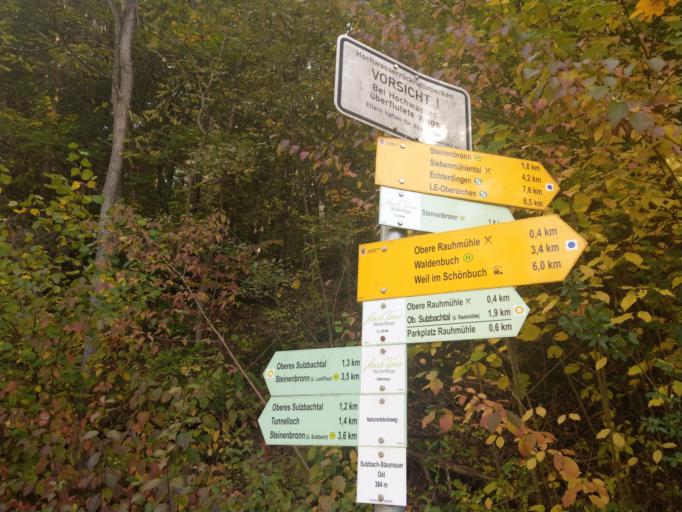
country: DE
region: Baden-Wuerttemberg
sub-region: Regierungsbezirk Stuttgart
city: Steinenbronn
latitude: 48.6535
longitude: 9.1047
